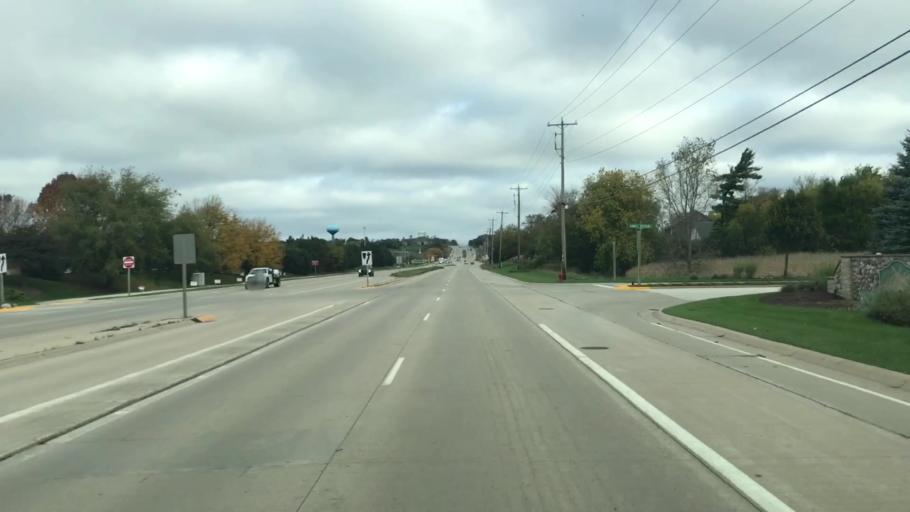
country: US
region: Wisconsin
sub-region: Waukesha County
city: Pewaukee
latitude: 43.0634
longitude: -88.2250
